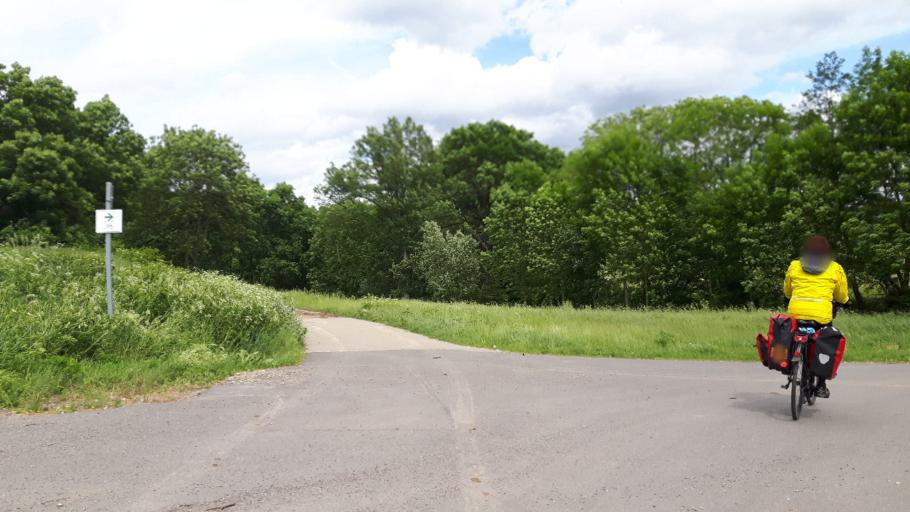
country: DE
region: Thuringia
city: Stadtilm
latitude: 50.7639
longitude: 11.0511
